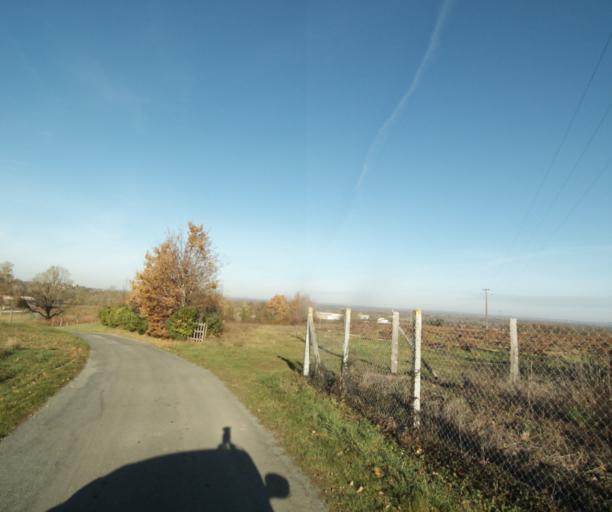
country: FR
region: Poitou-Charentes
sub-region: Departement de la Charente-Maritime
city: Burie
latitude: 45.7809
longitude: -0.4344
